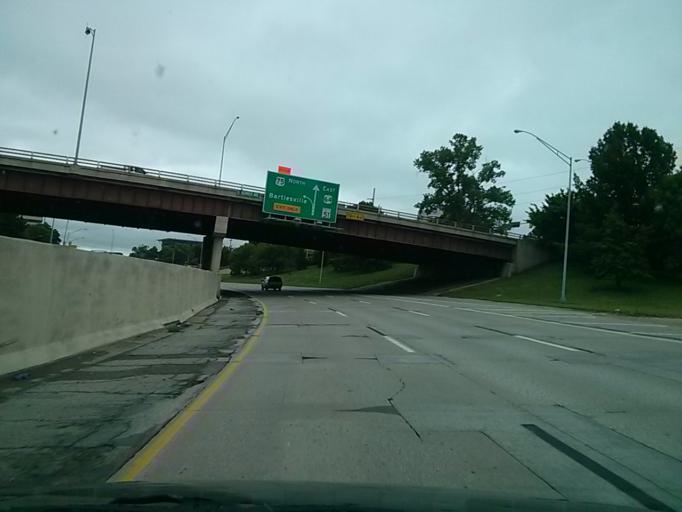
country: US
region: Oklahoma
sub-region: Tulsa County
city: Tulsa
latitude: 36.1444
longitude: -95.9931
